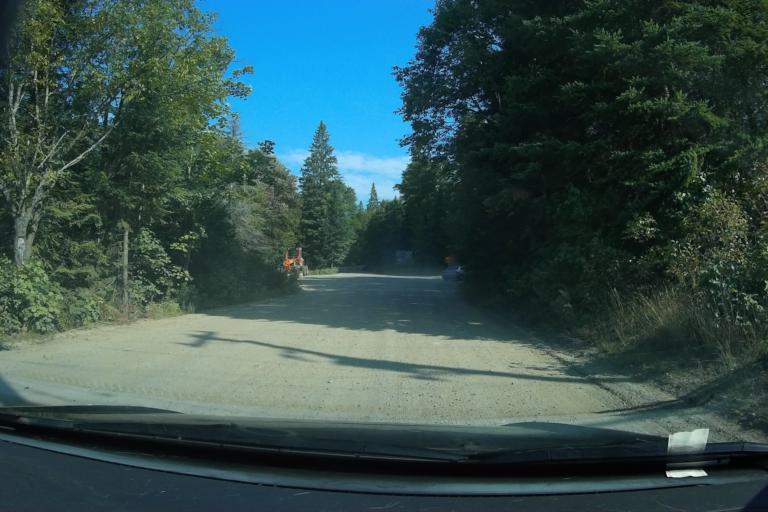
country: CA
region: Ontario
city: Huntsville
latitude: 45.5420
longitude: -78.6955
